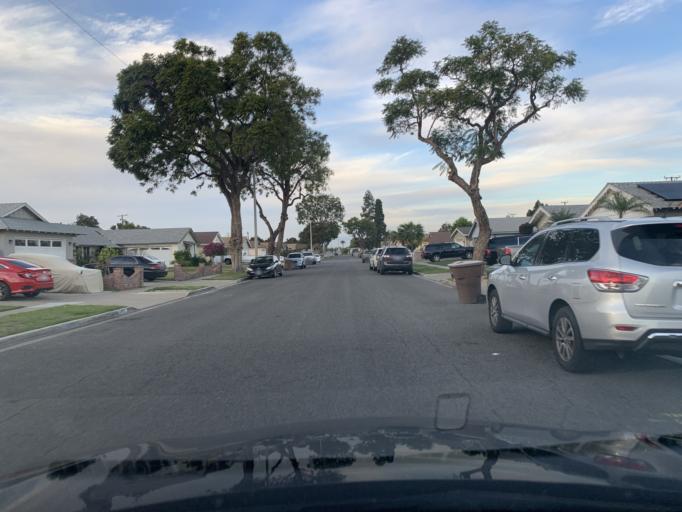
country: US
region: California
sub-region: Orange County
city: Garden Grove
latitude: 33.7796
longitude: -117.9274
